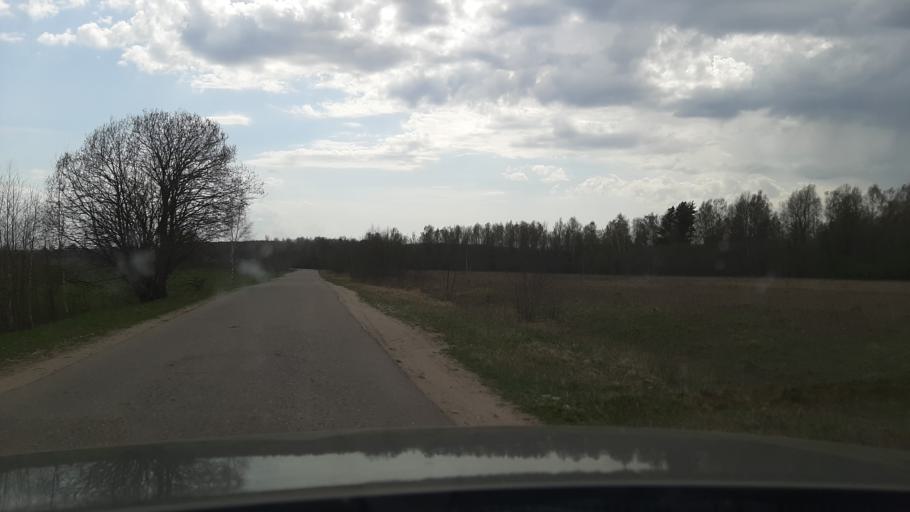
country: RU
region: Ivanovo
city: Furmanov
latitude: 57.3112
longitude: 41.1632
